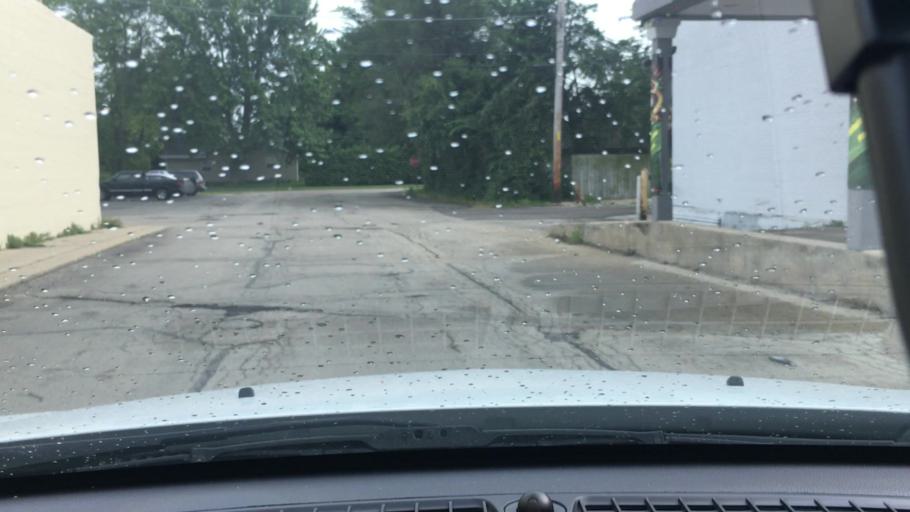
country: US
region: Illinois
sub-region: Ogle County
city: Rochelle
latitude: 41.9334
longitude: -89.0637
